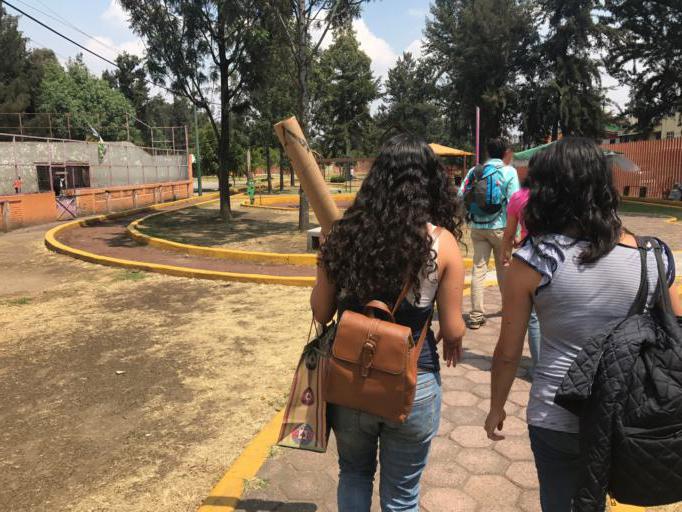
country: MX
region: Mexico City
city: Iztapalapa
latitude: 19.3088
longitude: -99.0839
